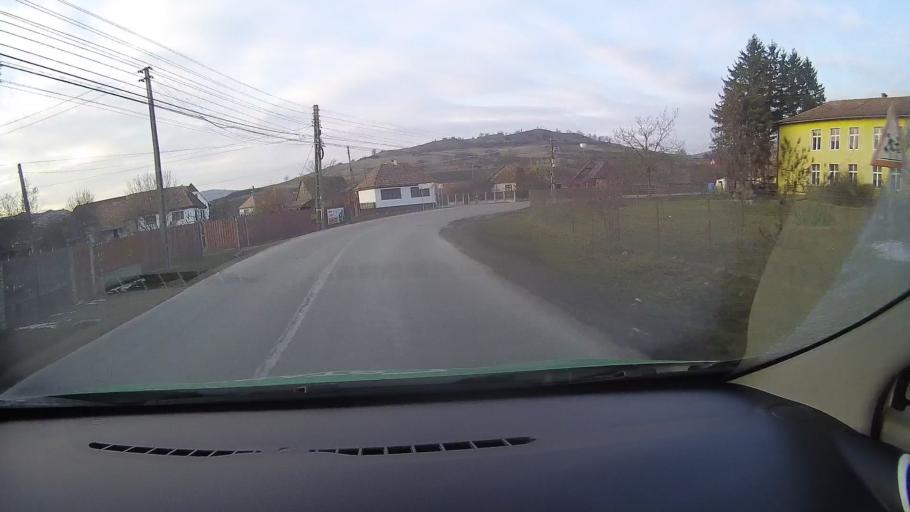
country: RO
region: Harghita
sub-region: Oras Cristuru Secuiesc
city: Cristuru Secuiesc
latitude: 46.3032
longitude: 25.0688
